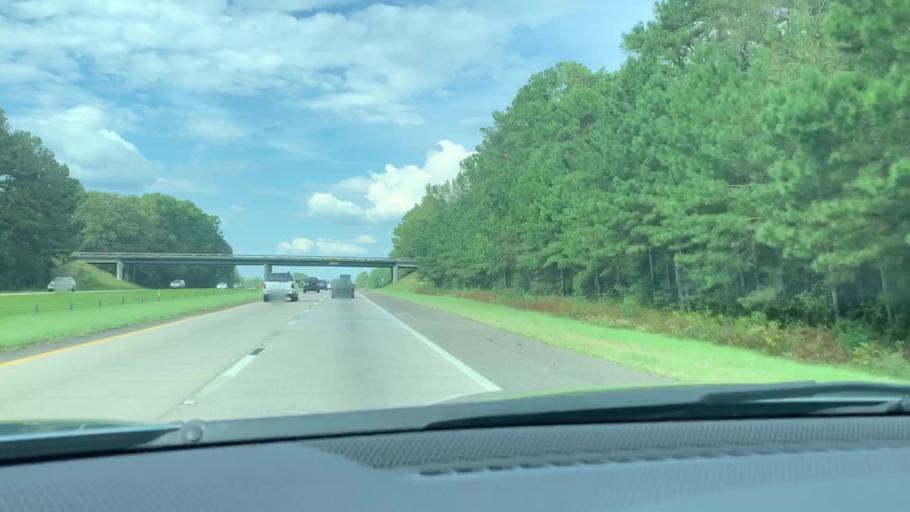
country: US
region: South Carolina
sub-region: Hampton County
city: Yemassee
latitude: 32.6774
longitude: -80.8823
